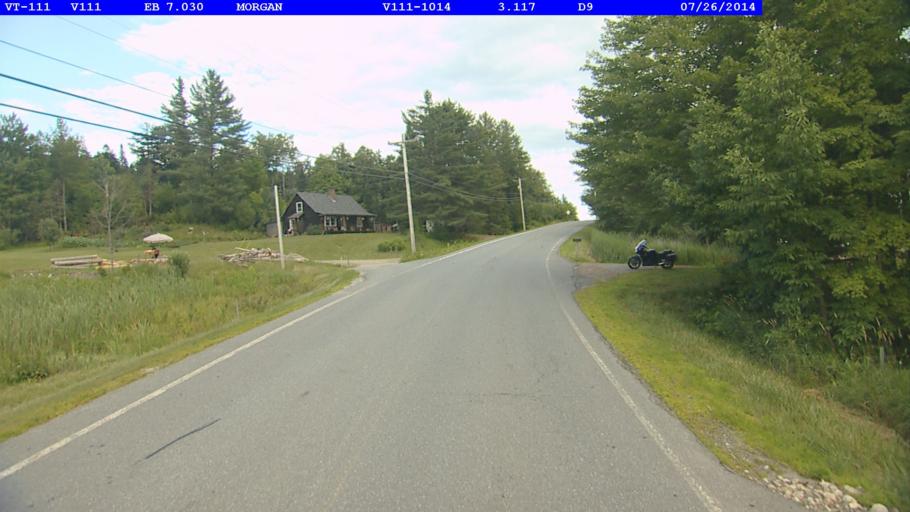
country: US
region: Vermont
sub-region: Orleans County
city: Newport
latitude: 44.9109
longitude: -72.0097
